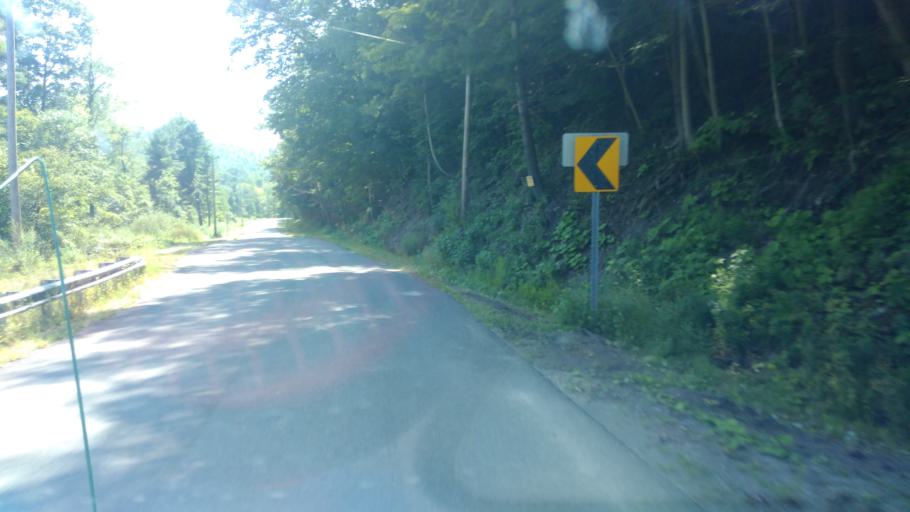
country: US
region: New York
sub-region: Steuben County
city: Canisteo
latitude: 42.3111
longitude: -77.6075
